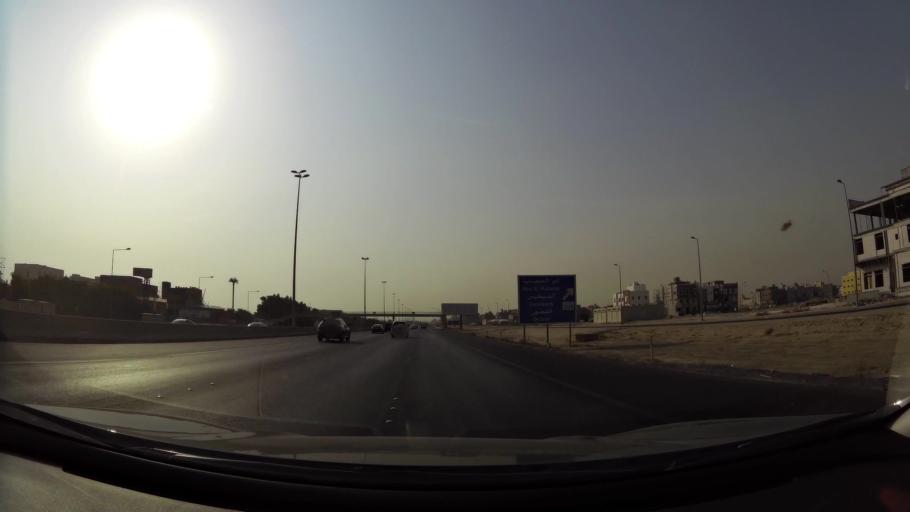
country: KW
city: Al Funaytis
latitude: 29.2205
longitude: 48.1007
